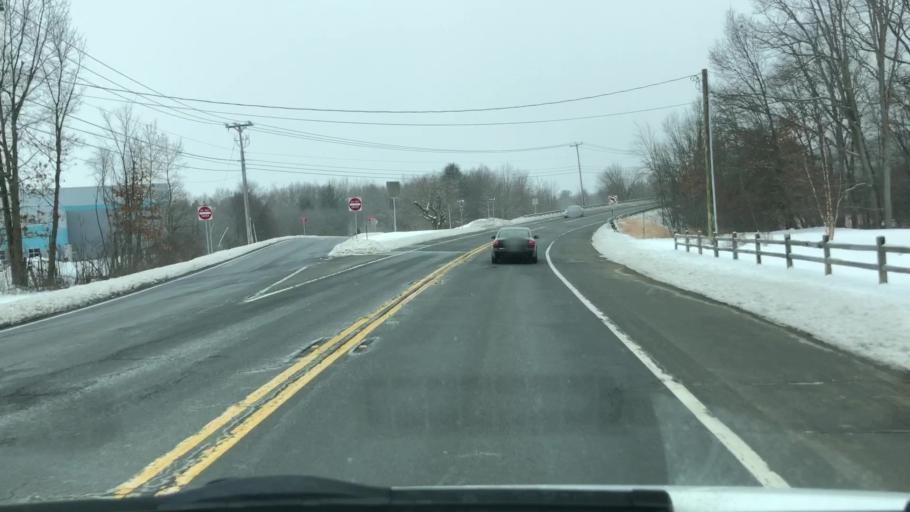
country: US
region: Massachusetts
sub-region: Hampshire County
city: Hatfield
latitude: 42.4001
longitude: -72.6263
